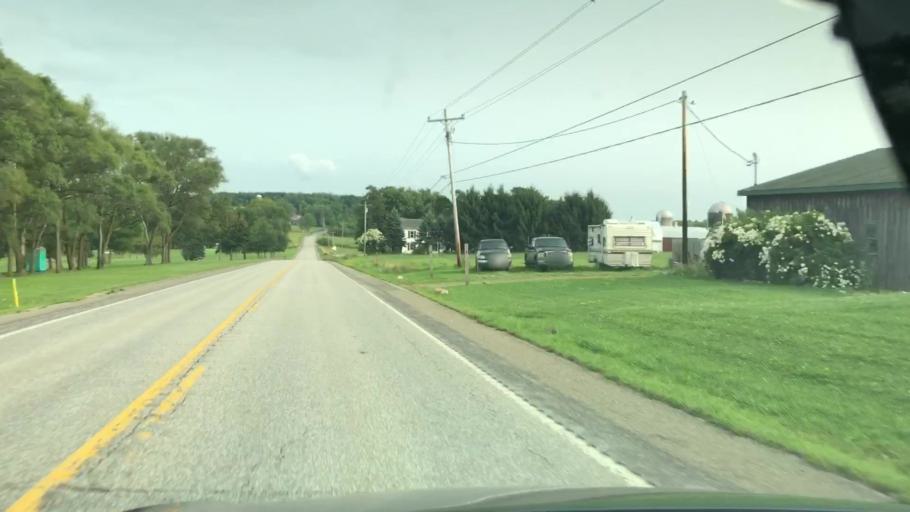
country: US
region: Pennsylvania
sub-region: Erie County
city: Union City
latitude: 41.8566
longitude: -79.8284
